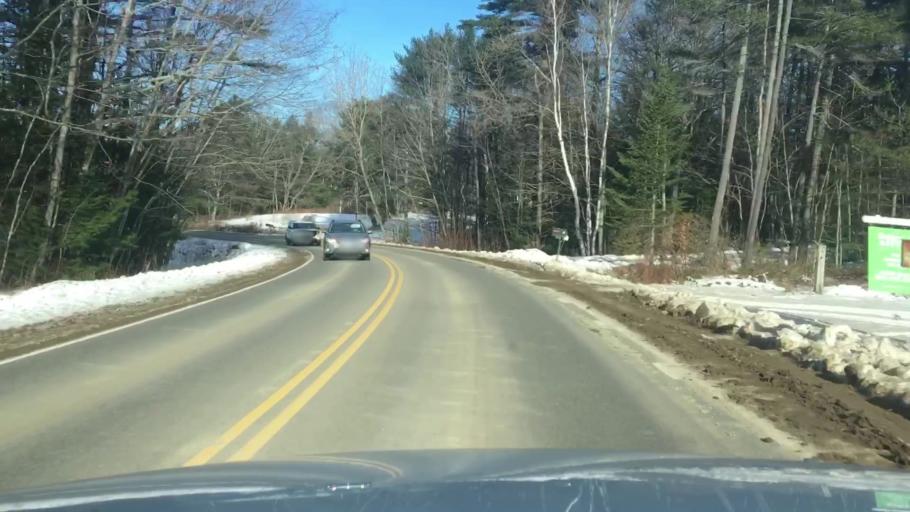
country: US
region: Maine
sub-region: Lincoln County
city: Wiscasset
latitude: 43.9715
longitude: -69.6699
